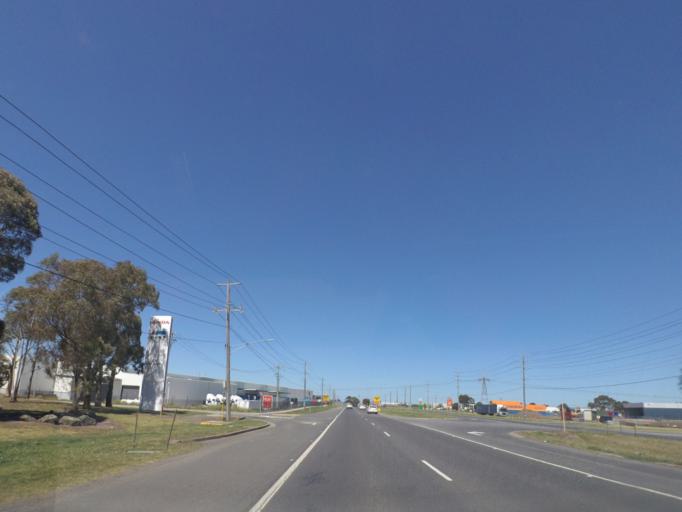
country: AU
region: Victoria
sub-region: Hume
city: Roxburgh Park
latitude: -37.6259
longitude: 144.9487
